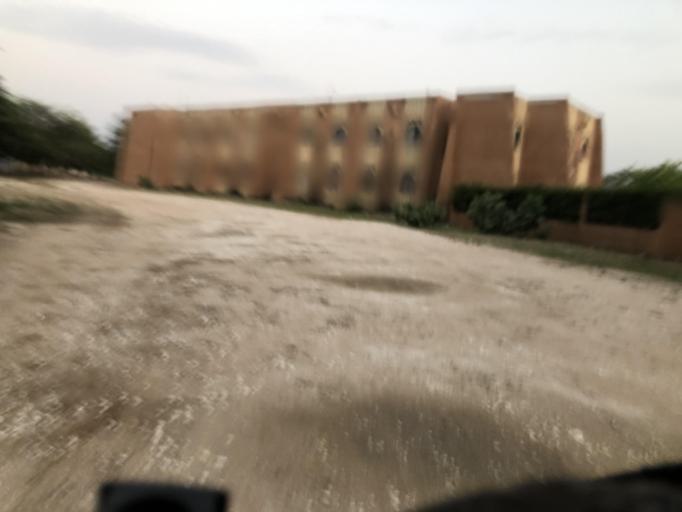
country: SN
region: Saint-Louis
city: Saint-Louis
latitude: 16.0646
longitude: -16.4272
